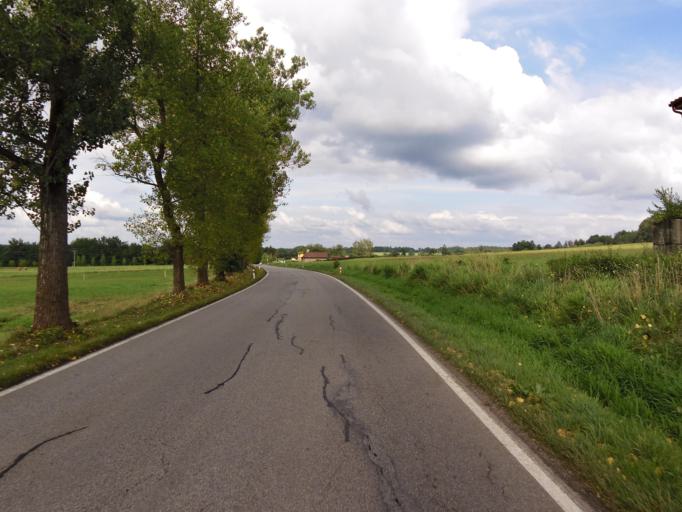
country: CZ
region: Jihocesky
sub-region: Okres Ceske Budejovice
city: Nove Hrady
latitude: 48.7979
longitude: 14.7900
